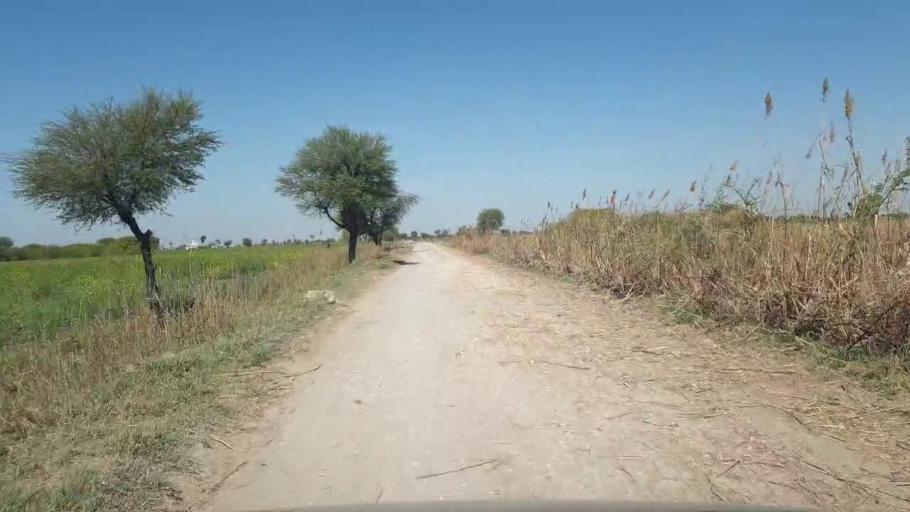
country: PK
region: Sindh
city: Dhoro Naro
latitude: 25.4408
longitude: 69.6170
